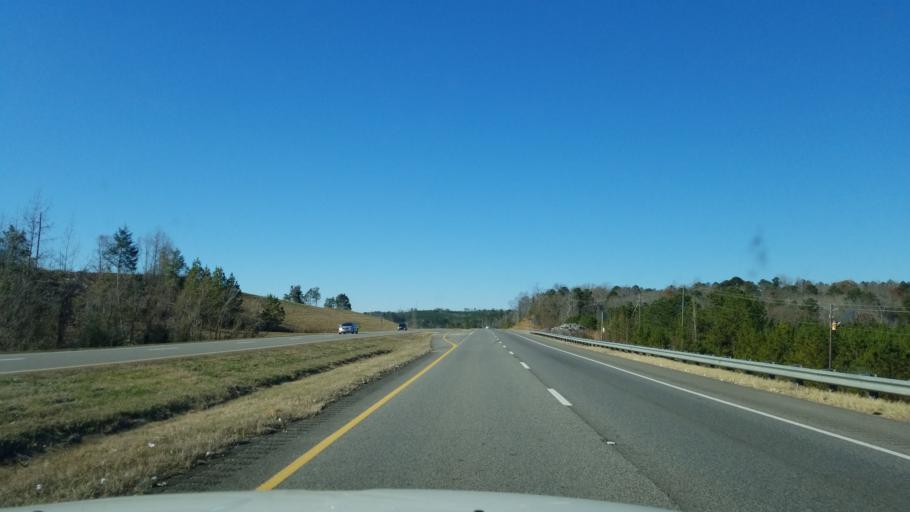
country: US
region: Alabama
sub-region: Tuscaloosa County
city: Northport
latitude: 33.2619
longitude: -87.7056
